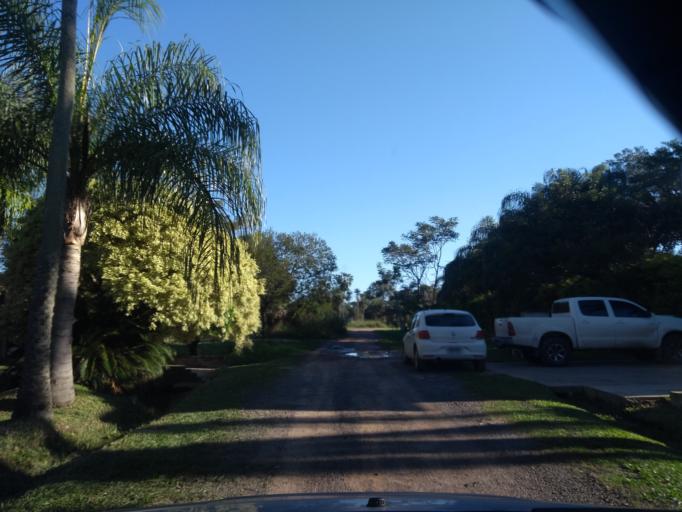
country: AR
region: Chaco
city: Barranqueras
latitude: -27.4394
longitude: -58.9081
